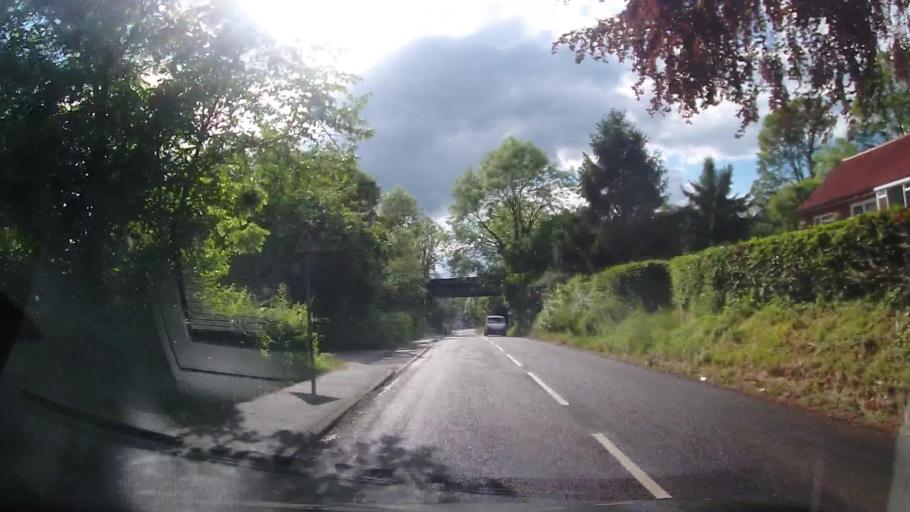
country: GB
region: England
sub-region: Telford and Wrekin
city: Ironbridge
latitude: 52.6318
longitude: -2.5002
